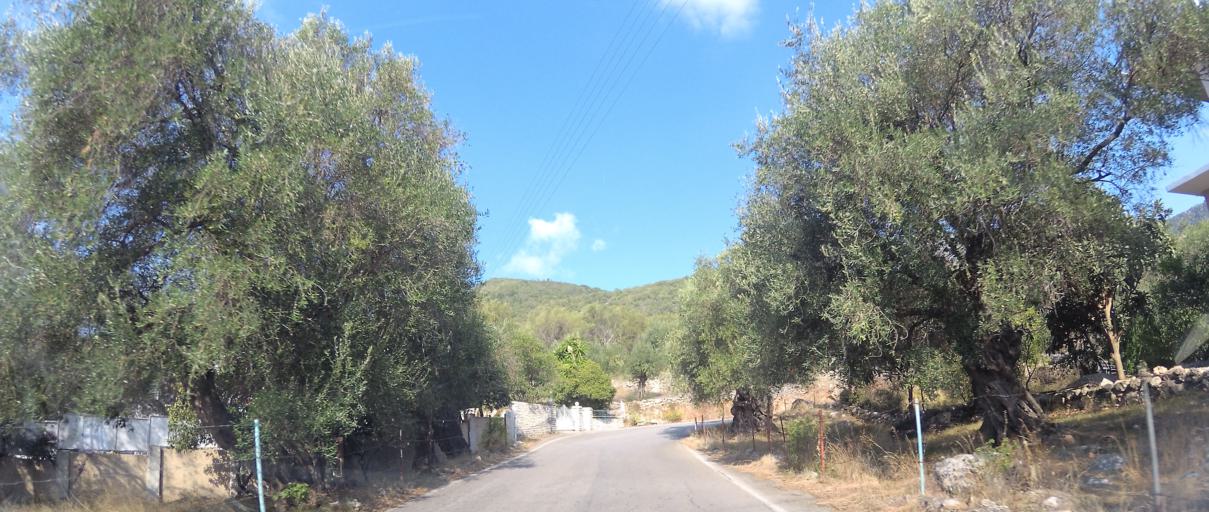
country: GR
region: Ionian Islands
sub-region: Nomos Kerkyras
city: Kontokali
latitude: 39.7101
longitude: 19.8451
